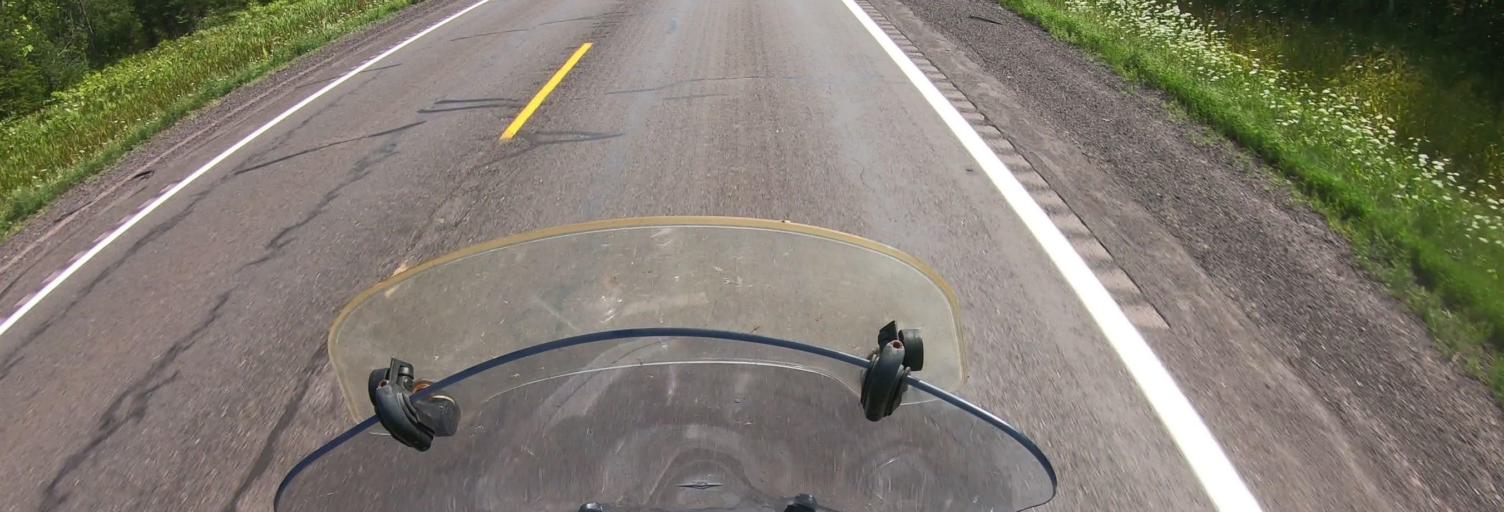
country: US
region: Michigan
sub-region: Ontonagon County
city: Ontonagon
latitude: 46.6602
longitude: -89.1718
